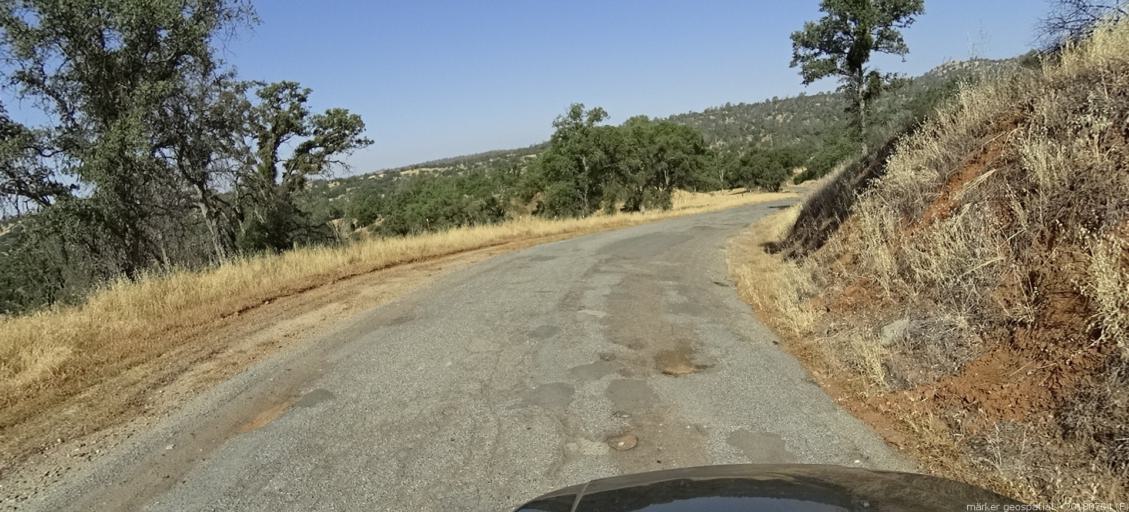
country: US
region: California
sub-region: Madera County
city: Yosemite Lakes
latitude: 37.1136
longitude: -119.6456
